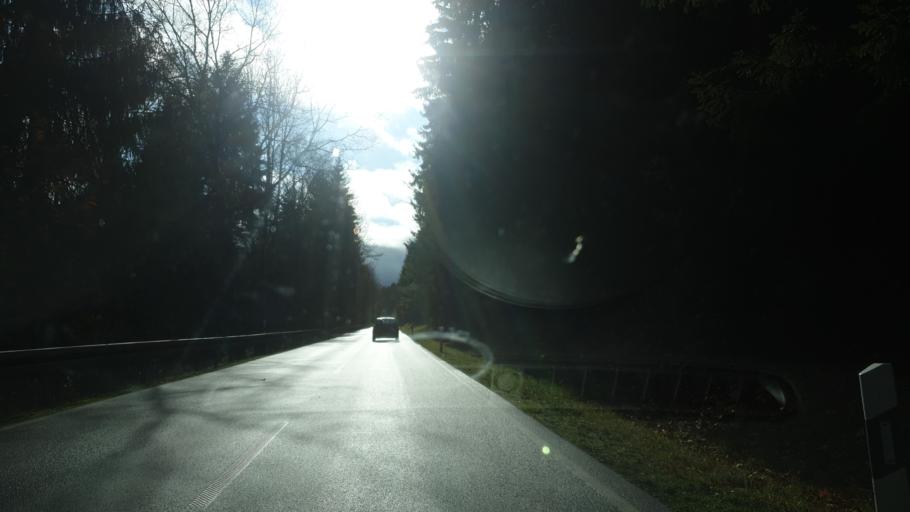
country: DE
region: Saxony
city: Zschorlau
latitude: 50.5392
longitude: 12.6550
